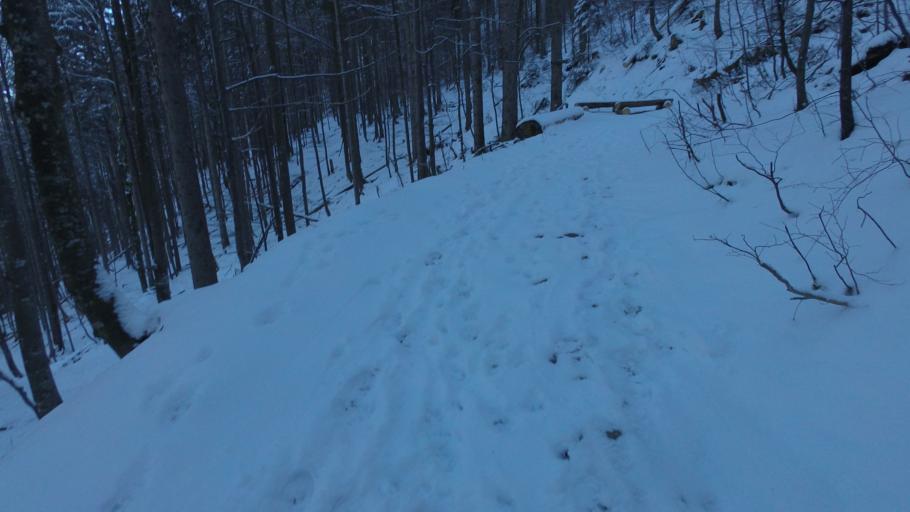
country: DE
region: Bavaria
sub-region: Upper Bavaria
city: Bergen
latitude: 47.7200
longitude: 12.5727
